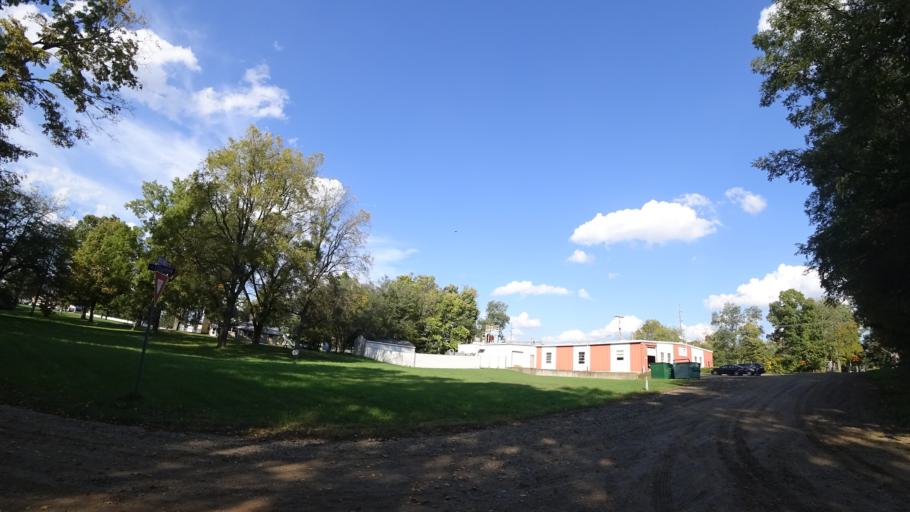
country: US
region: Michigan
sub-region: Saint Joseph County
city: Three Rivers
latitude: 41.9536
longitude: -85.6407
